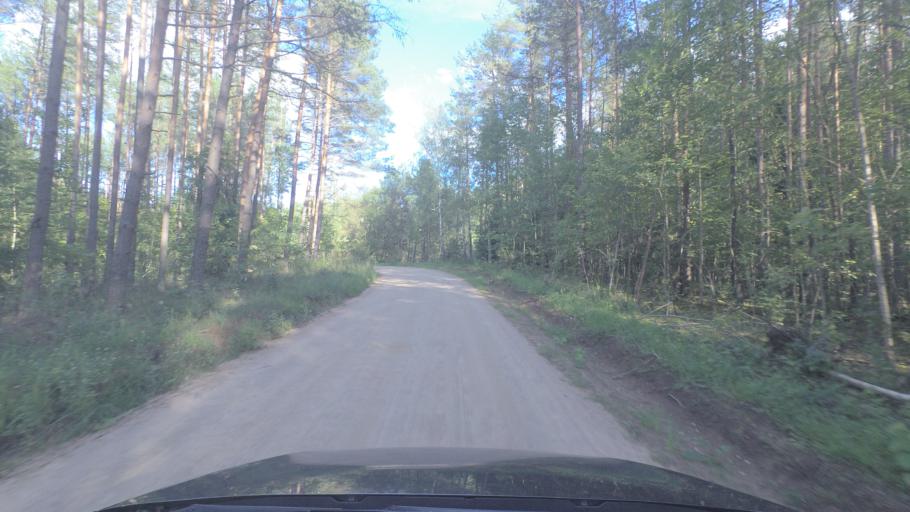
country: LT
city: Pabrade
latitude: 55.1397
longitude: 25.7270
